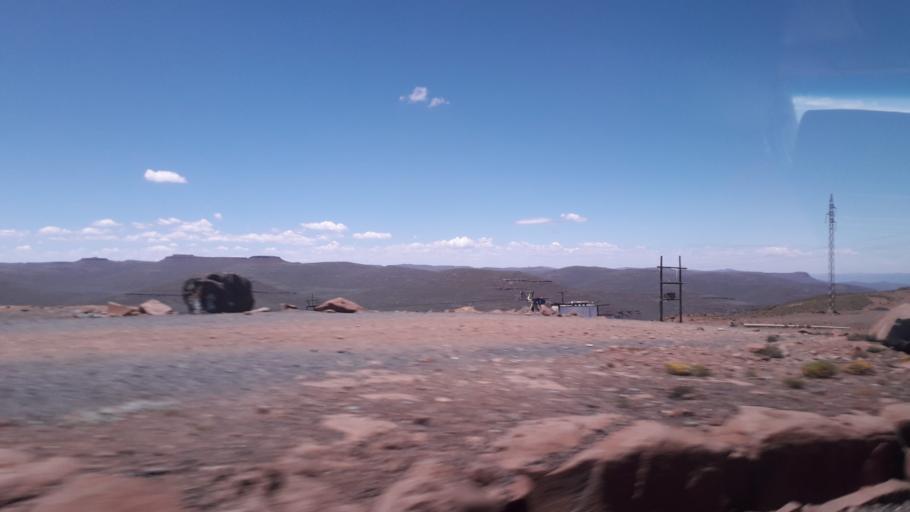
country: ZA
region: Orange Free State
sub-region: Thabo Mofutsanyana District Municipality
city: Phuthaditjhaba
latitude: -28.8157
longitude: 28.7200
